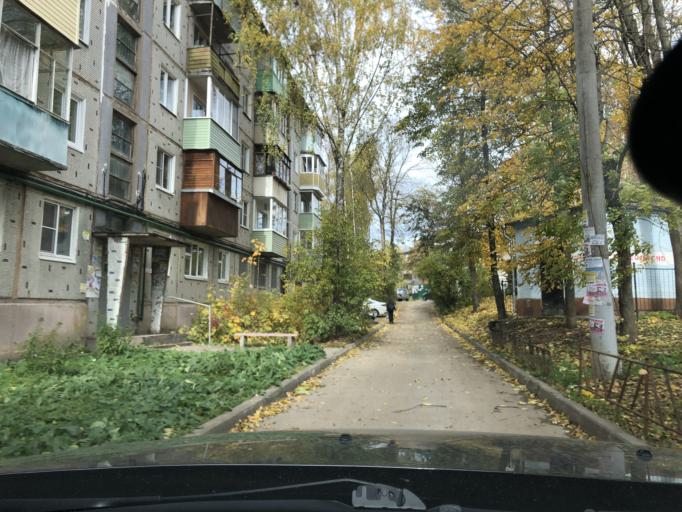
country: RU
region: Tula
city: Mendeleyevskiy
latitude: 54.1782
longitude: 37.5681
